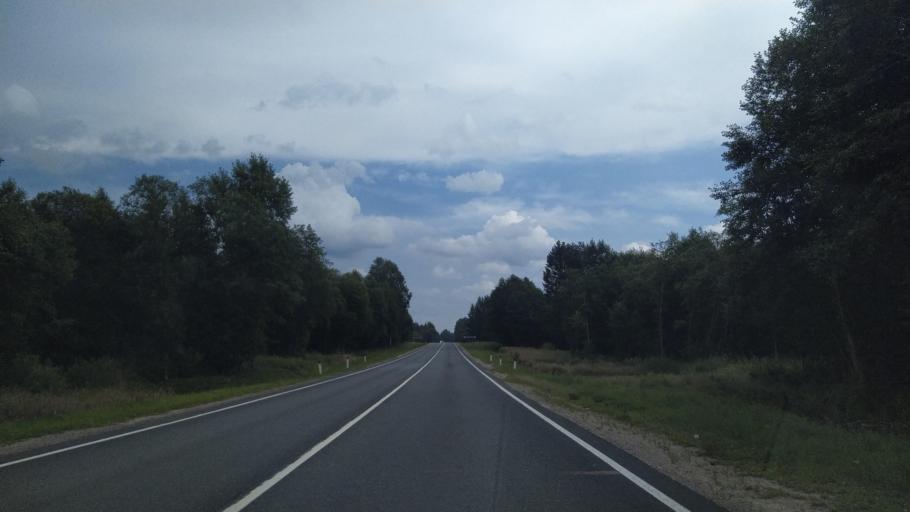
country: RU
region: Pskov
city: Pskov
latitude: 57.8144
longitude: 28.6672
